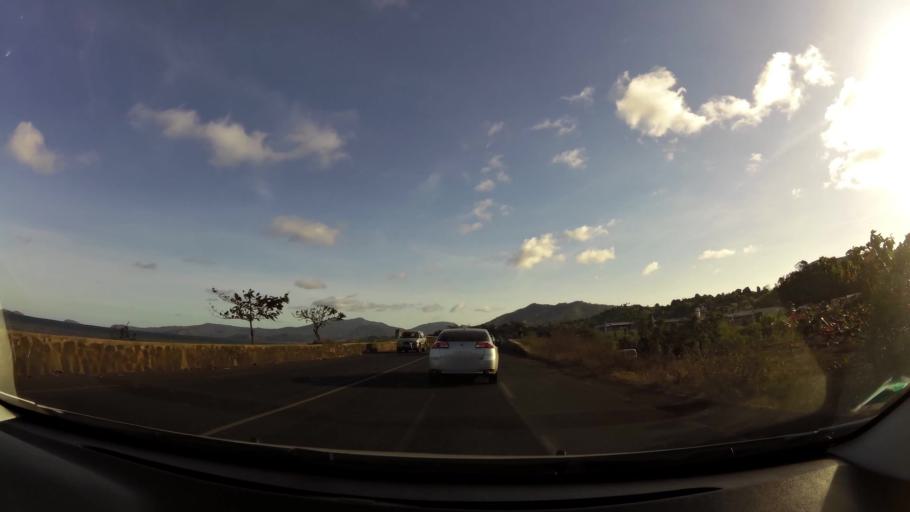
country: YT
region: Mamoudzou
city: Mamoudzou
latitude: -12.7906
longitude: 45.2232
